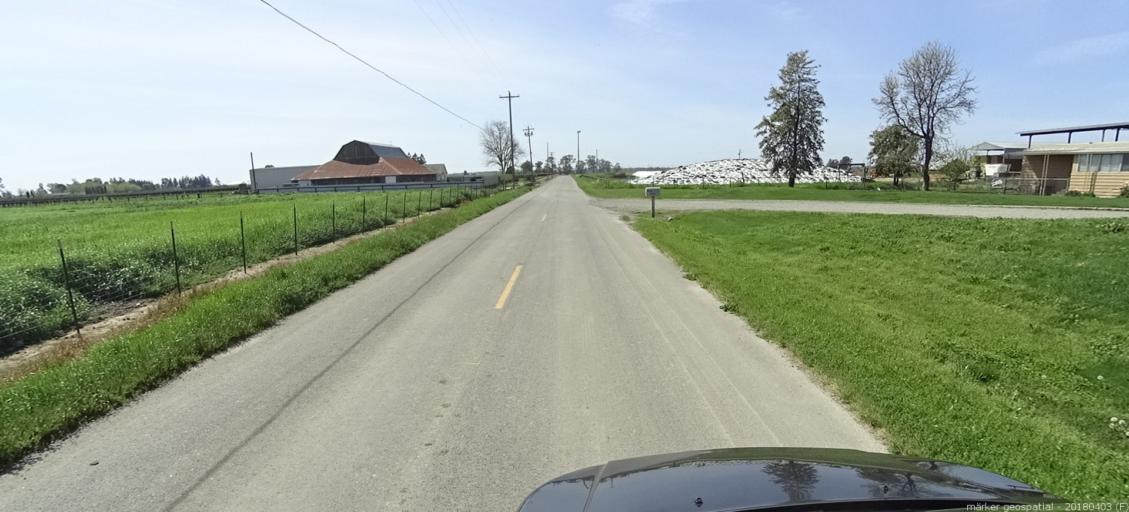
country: US
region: California
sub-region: Sacramento County
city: Herald
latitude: 38.3363
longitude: -121.2873
